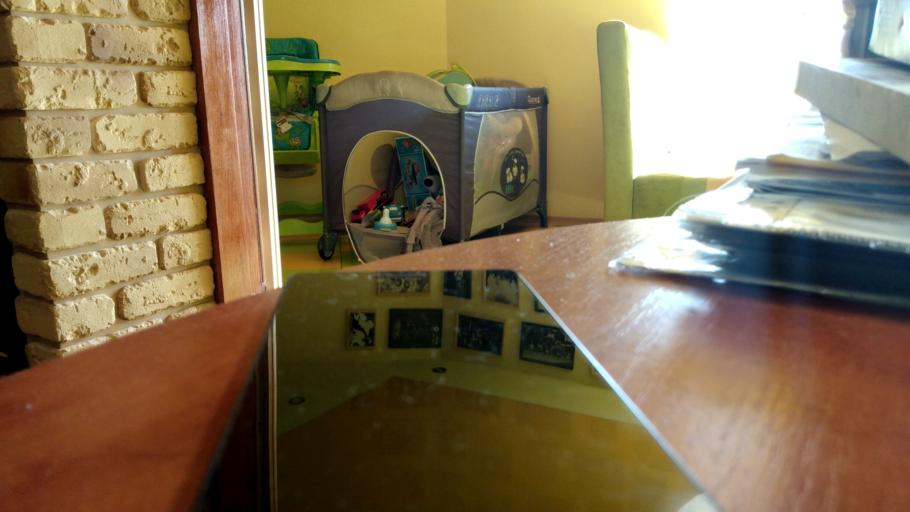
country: RU
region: Penza
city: Serdobsk
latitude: 52.3530
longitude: 44.3608
